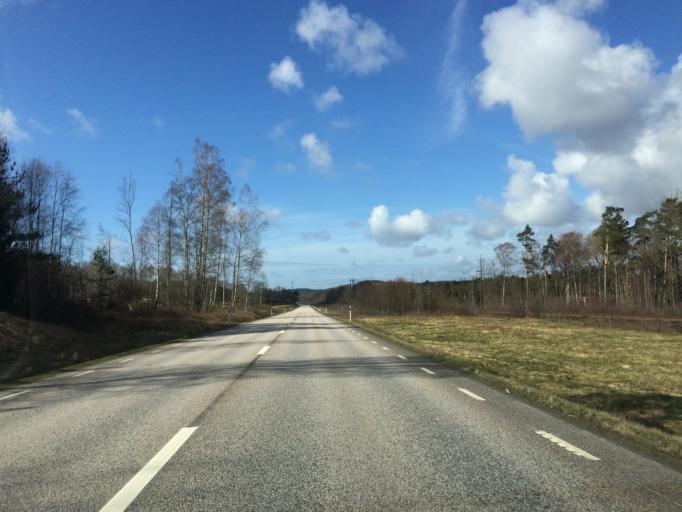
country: SE
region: Halland
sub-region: Laholms Kommun
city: Knared
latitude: 56.5056
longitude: 13.3487
